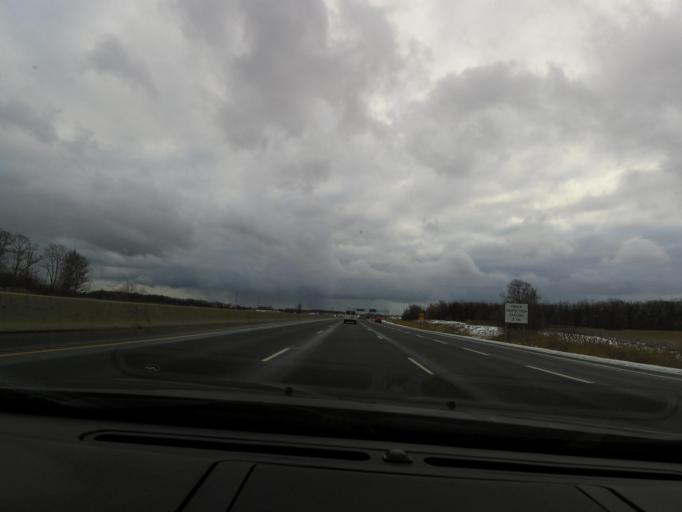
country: CA
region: Ontario
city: Burlington
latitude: 43.4527
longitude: -79.7873
